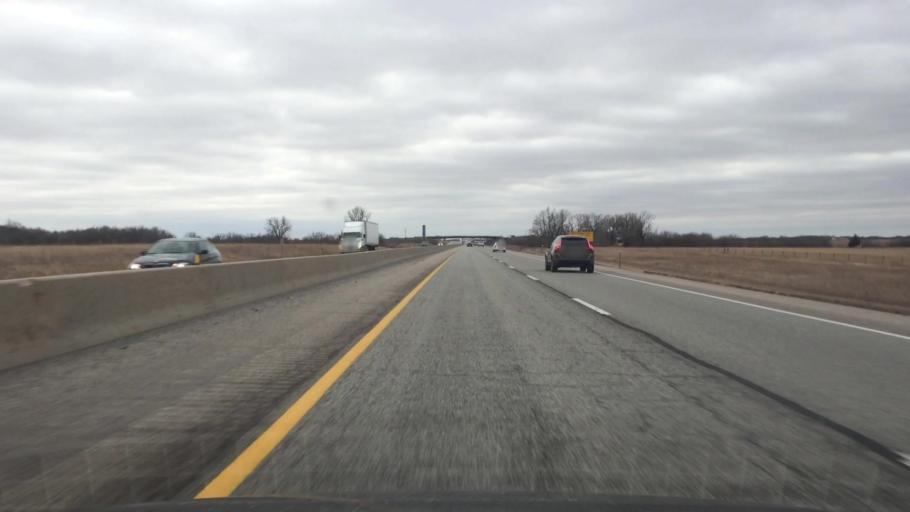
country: US
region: Kansas
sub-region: Butler County
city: El Dorado
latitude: 38.0335
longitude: -96.6548
